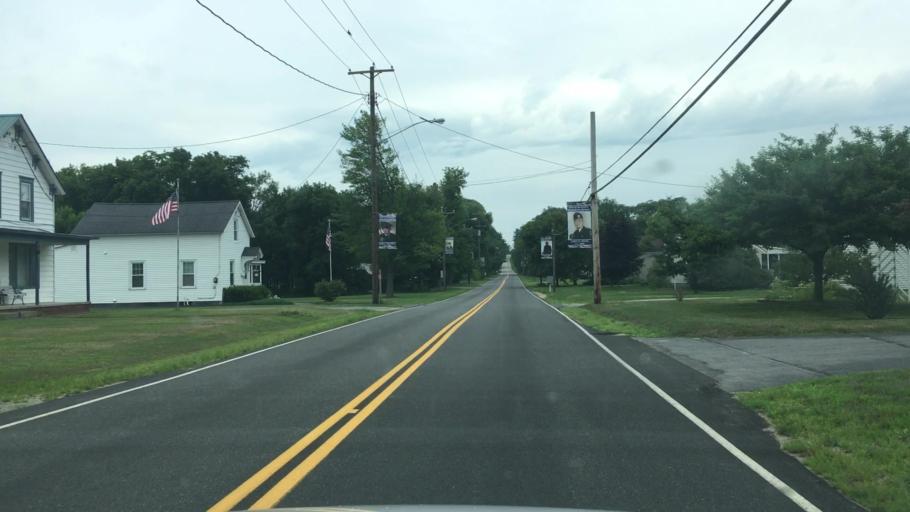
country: US
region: New York
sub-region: Essex County
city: Keeseville
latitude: 44.5020
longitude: -73.4746
